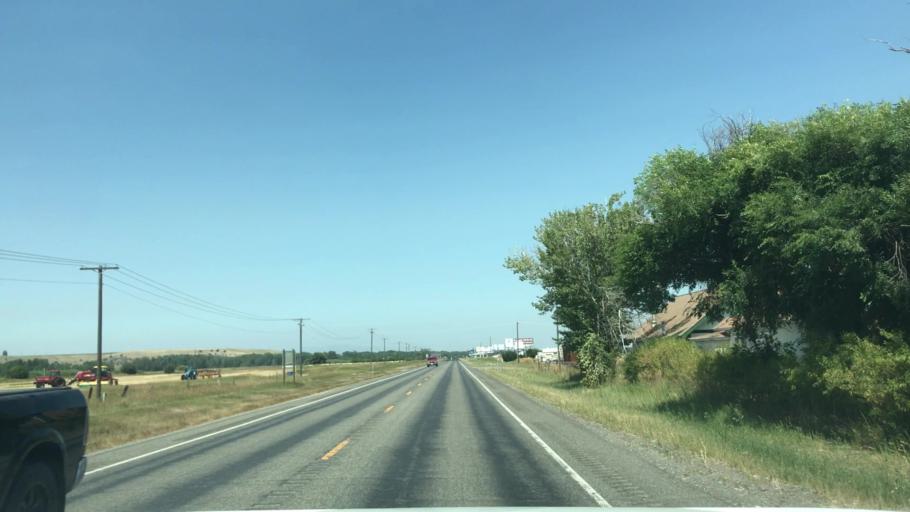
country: US
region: Montana
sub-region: Gallatin County
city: Four Corners
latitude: 45.6275
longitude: -111.1969
